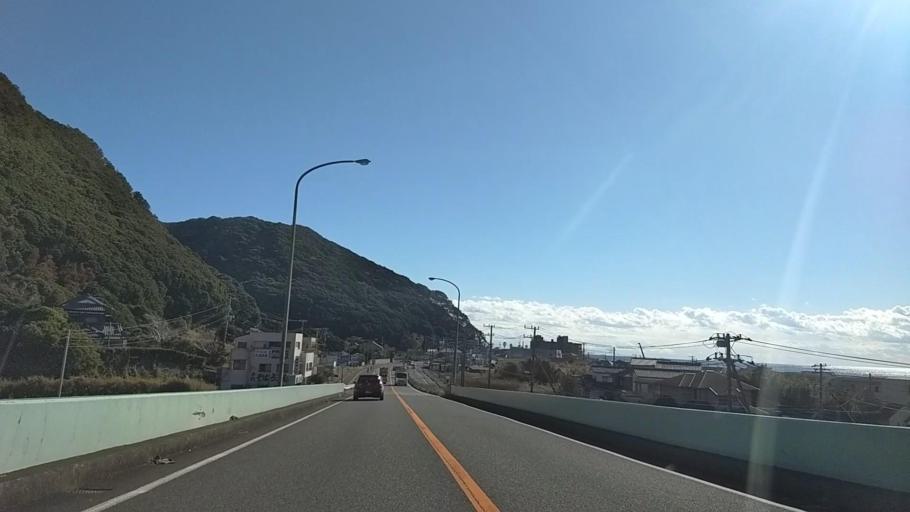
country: JP
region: Chiba
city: Kawaguchi
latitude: 35.1262
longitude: 140.1708
